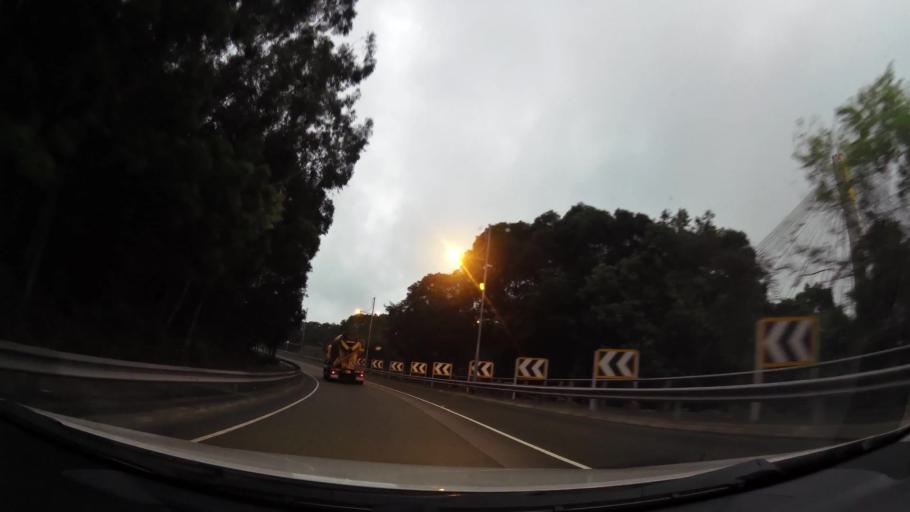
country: HK
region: Tsuen Wan
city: Tsuen Wan
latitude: 22.3595
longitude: 114.0837
